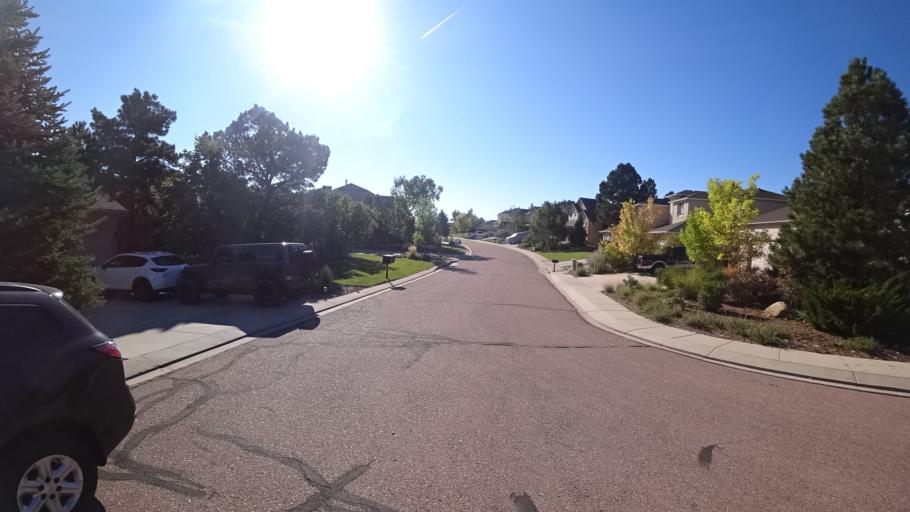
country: US
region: Colorado
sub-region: El Paso County
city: Colorado Springs
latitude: 38.9044
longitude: -104.7919
